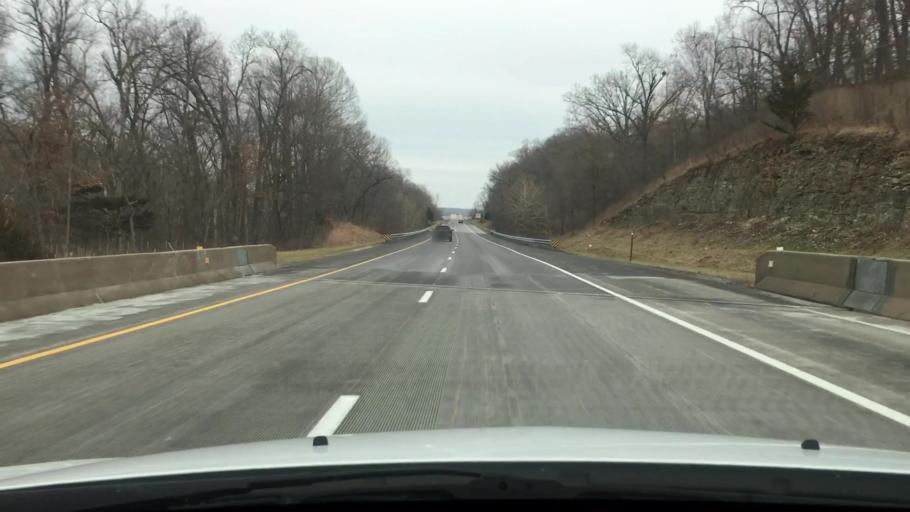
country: US
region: Illinois
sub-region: Pike County
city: Griggsville
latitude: 39.6824
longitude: -90.6524
